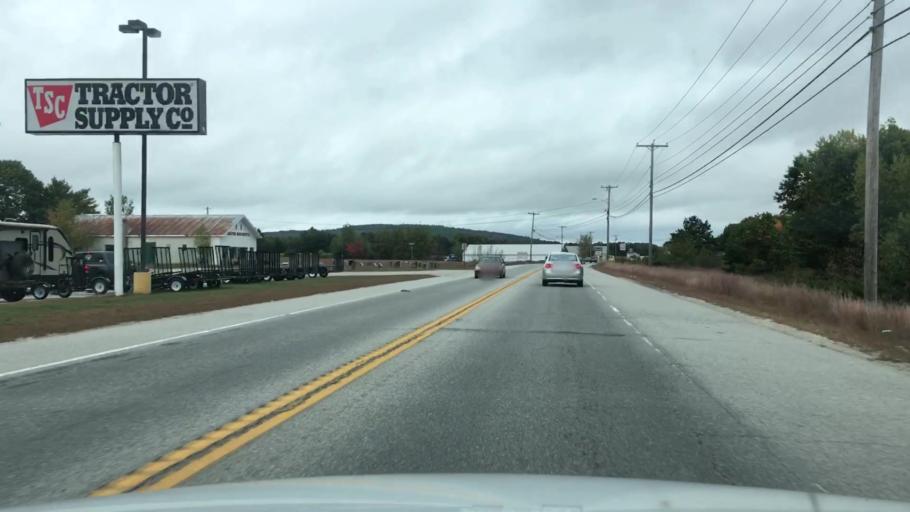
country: US
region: Maine
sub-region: Oxford County
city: Oxford
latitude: 44.1755
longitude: -70.5130
